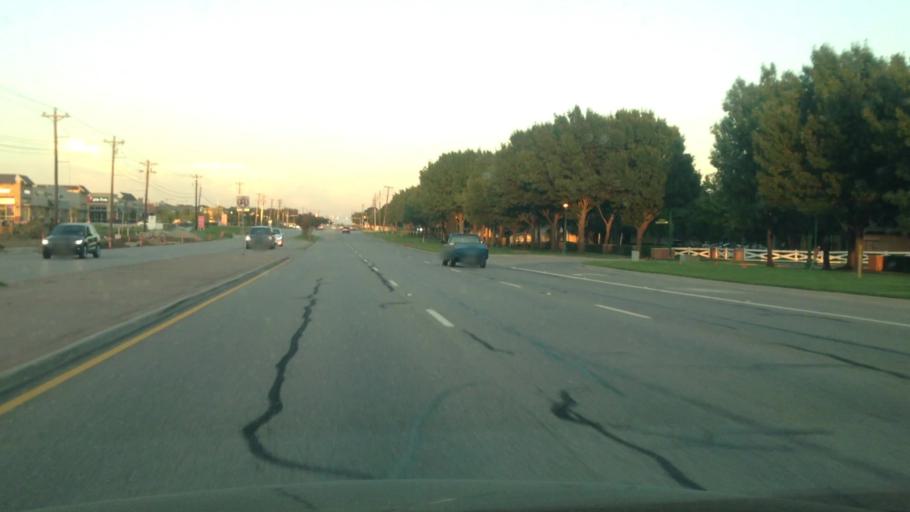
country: US
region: Texas
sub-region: Tarrant County
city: Keller
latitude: 32.9343
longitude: -97.2236
